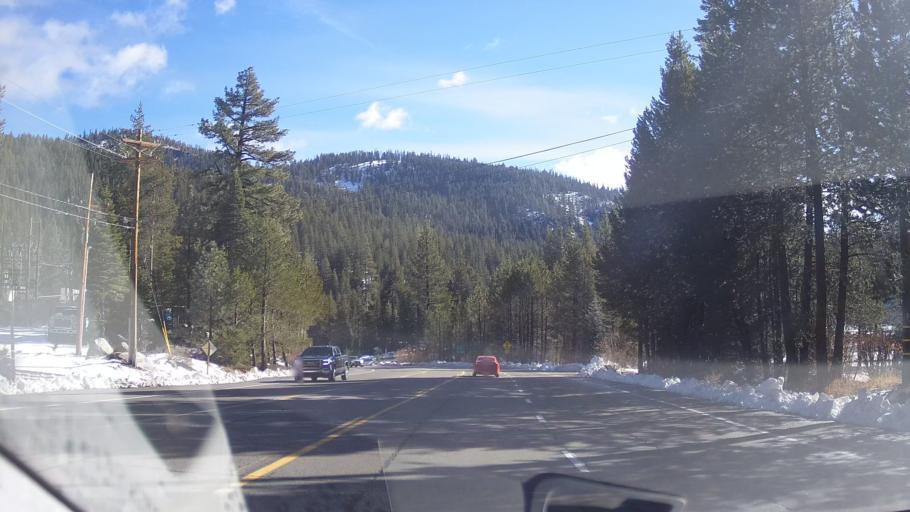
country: US
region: California
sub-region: Placer County
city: Sunnyside-Tahoe City
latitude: 39.2058
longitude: -120.2027
